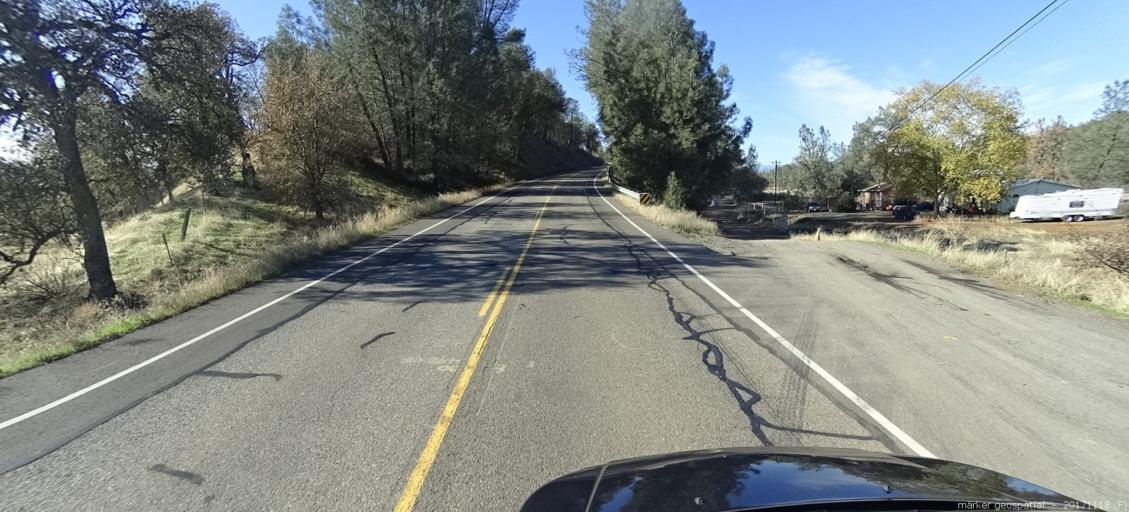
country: US
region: California
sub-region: Shasta County
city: Anderson
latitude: 40.4412
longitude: -122.3186
